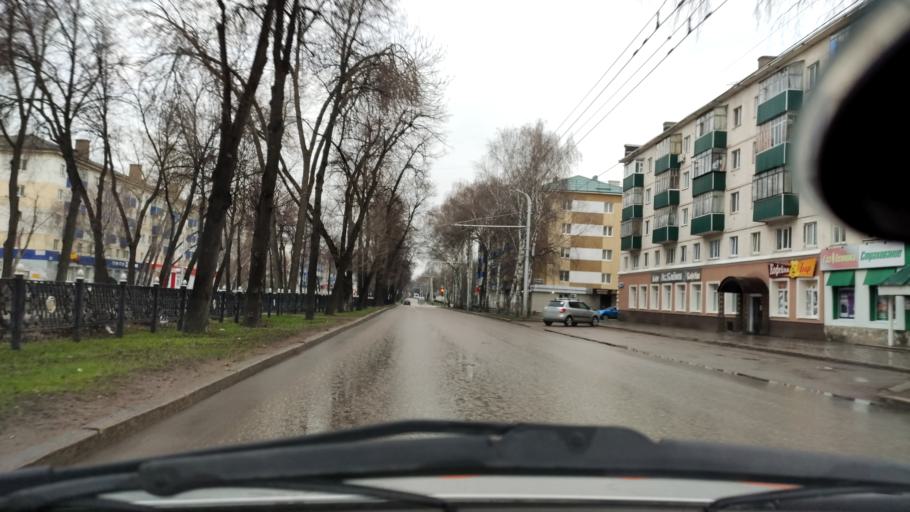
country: RU
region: Bashkortostan
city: Sterlitamak
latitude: 53.6406
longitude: 55.9396
